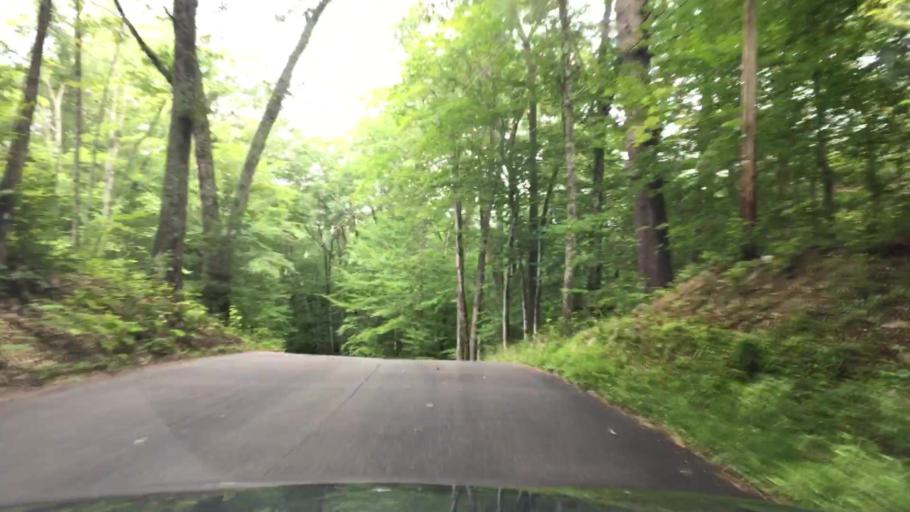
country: US
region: New Hampshire
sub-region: Carroll County
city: Sandwich
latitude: 43.7867
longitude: -71.4712
